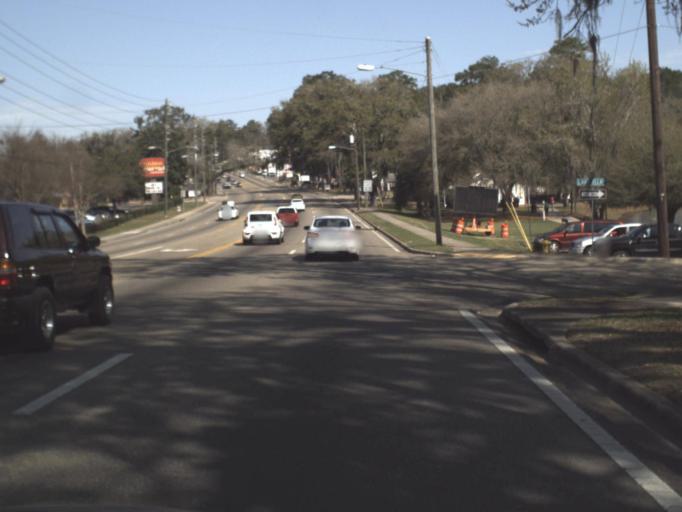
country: US
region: Florida
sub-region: Leon County
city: Tallahassee
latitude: 30.4597
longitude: -84.2809
